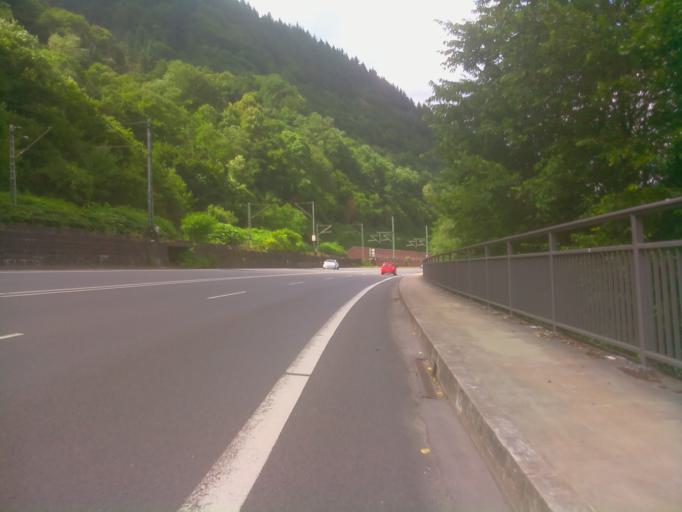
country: DE
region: Baden-Wuerttemberg
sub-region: Karlsruhe Region
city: Neckargemund
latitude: 49.3950
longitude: 8.7747
